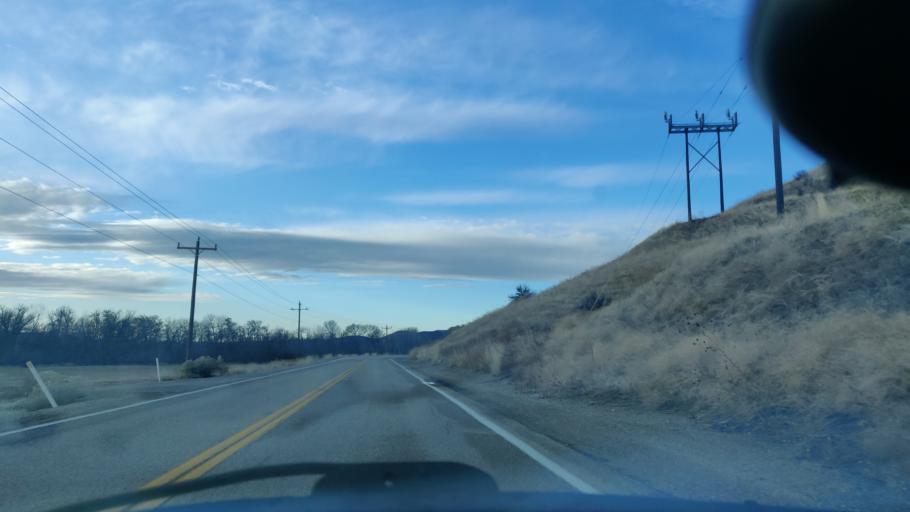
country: US
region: Idaho
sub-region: Ada County
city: Garden City
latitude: 43.7257
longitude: -116.2480
